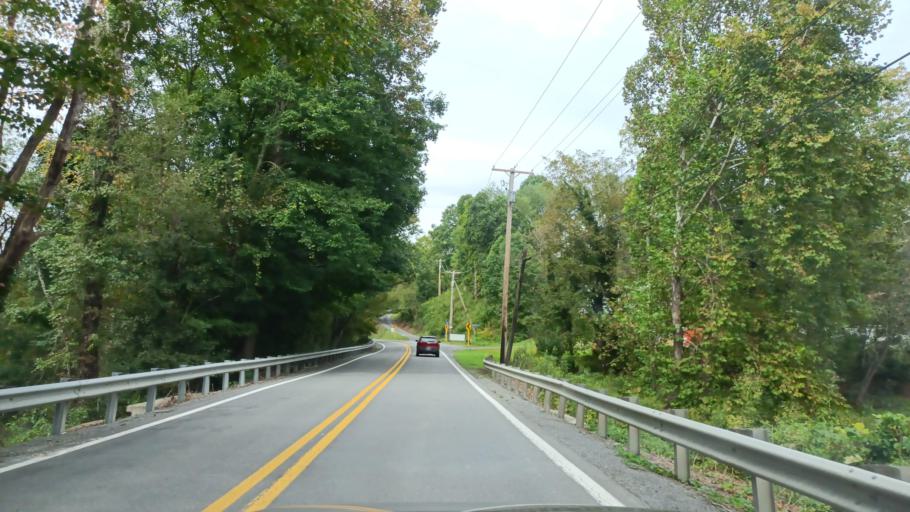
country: US
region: West Virginia
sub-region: Taylor County
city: Grafton
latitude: 39.3347
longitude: -79.8727
